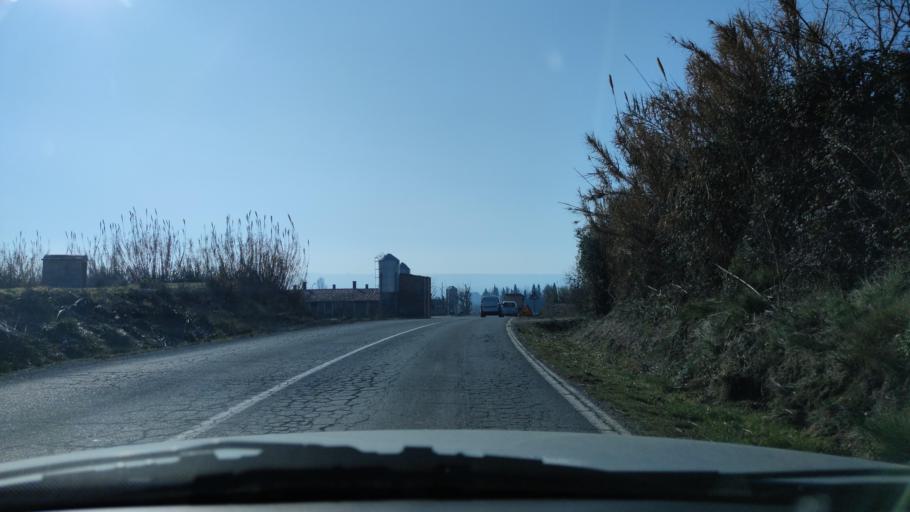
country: ES
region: Catalonia
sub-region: Provincia de Lleida
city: Juneda
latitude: 41.5631
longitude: 0.7481
